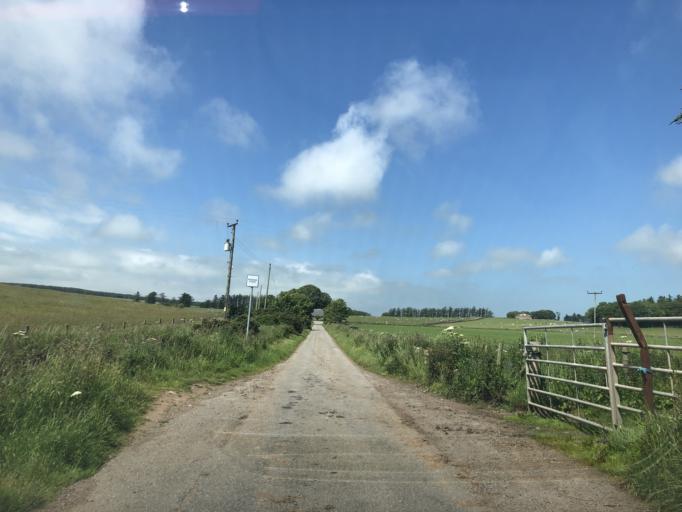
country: GB
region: Scotland
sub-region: Aberdeenshire
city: Stonehaven
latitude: 56.9187
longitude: -2.2072
